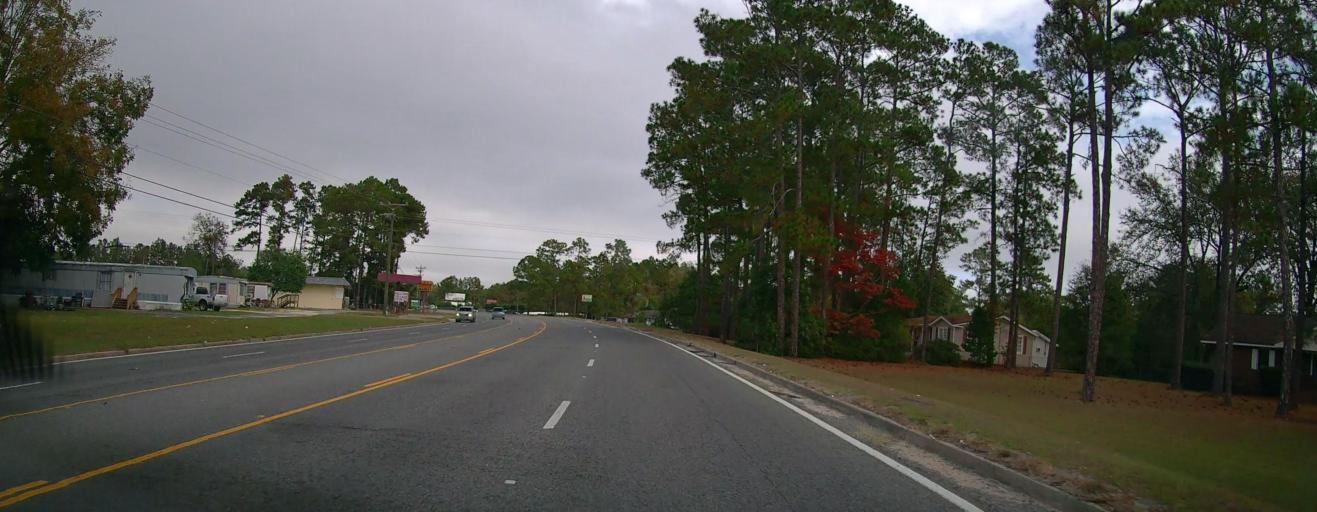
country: US
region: Georgia
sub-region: Tift County
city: Unionville
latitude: 31.3940
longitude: -83.5374
